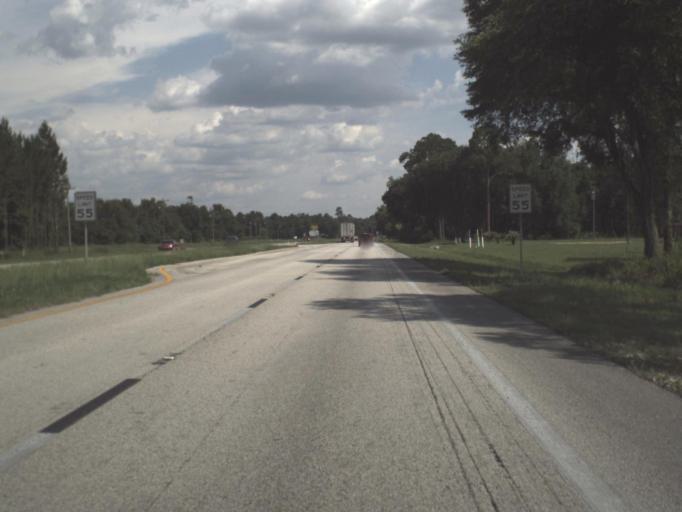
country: US
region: Florida
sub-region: Alachua County
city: Hawthorne
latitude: 29.6071
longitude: -82.0897
